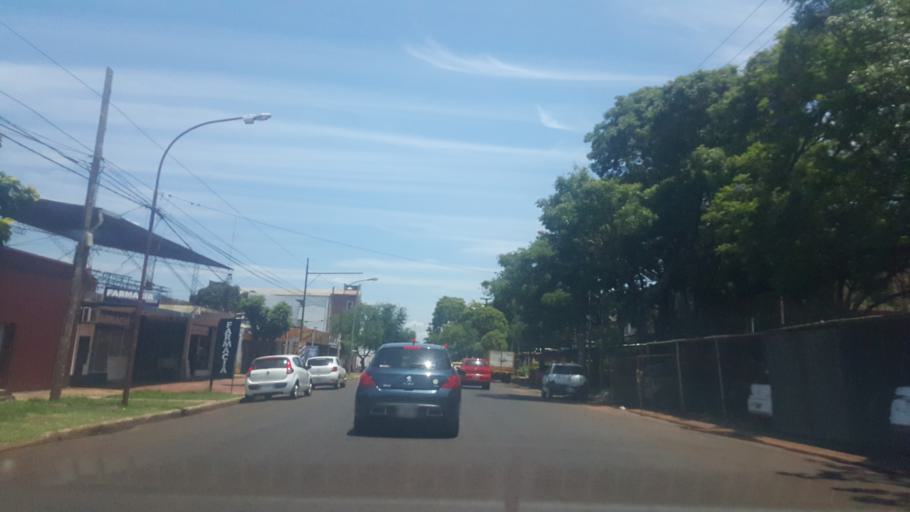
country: AR
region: Misiones
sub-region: Departamento de Capital
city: Posadas
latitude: -27.3959
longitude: -55.9053
